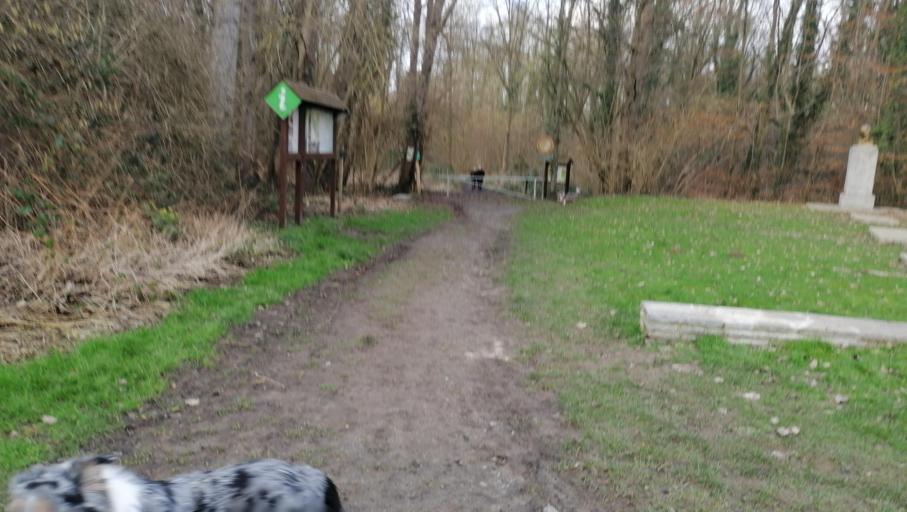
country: FR
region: Nord-Pas-de-Calais
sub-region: Departement du Nord
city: Quievrechain
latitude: 50.3460
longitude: 3.7040
